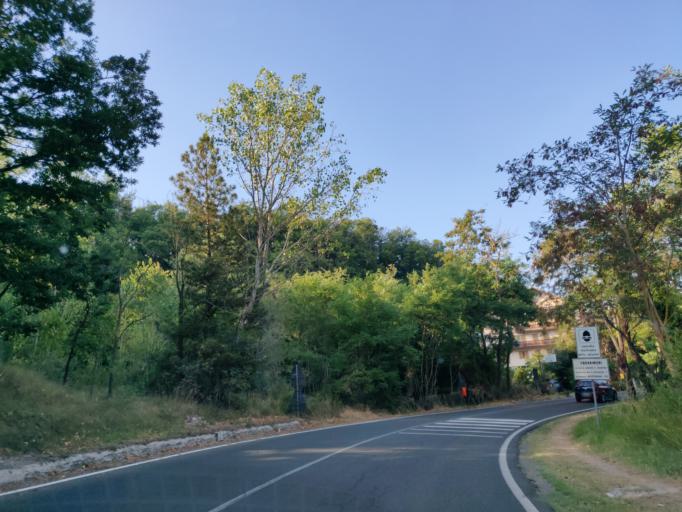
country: IT
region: Tuscany
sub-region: Provincia di Siena
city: Abbadia San Salvatore
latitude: 42.8737
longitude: 11.6828
